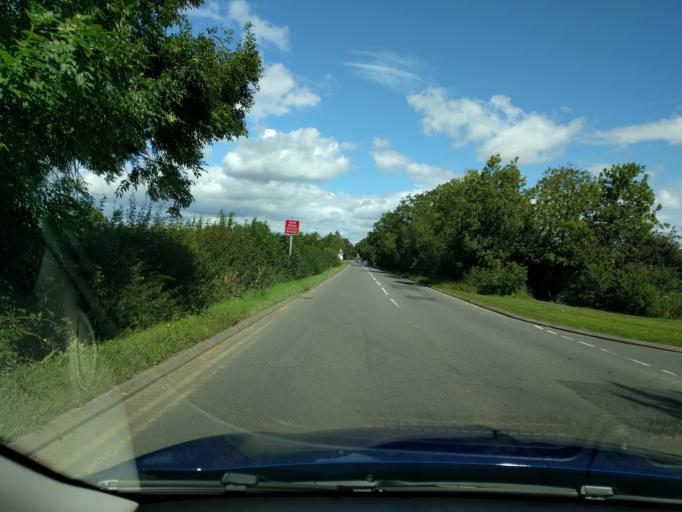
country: GB
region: England
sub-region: Gloucestershire
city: Mickleton
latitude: 52.1220
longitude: -1.7541
